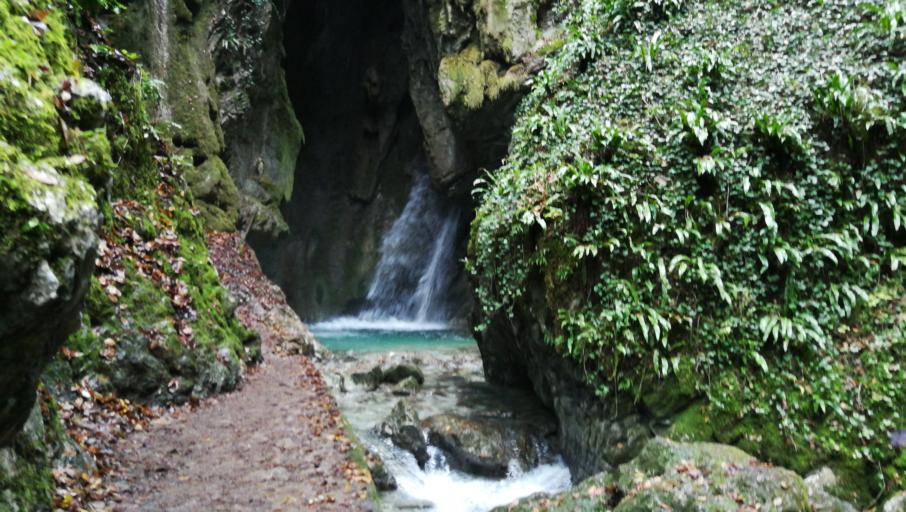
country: IT
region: Trentino-Alto Adige
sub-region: Provincia di Trento
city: Creto
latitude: 45.9000
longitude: 10.6714
